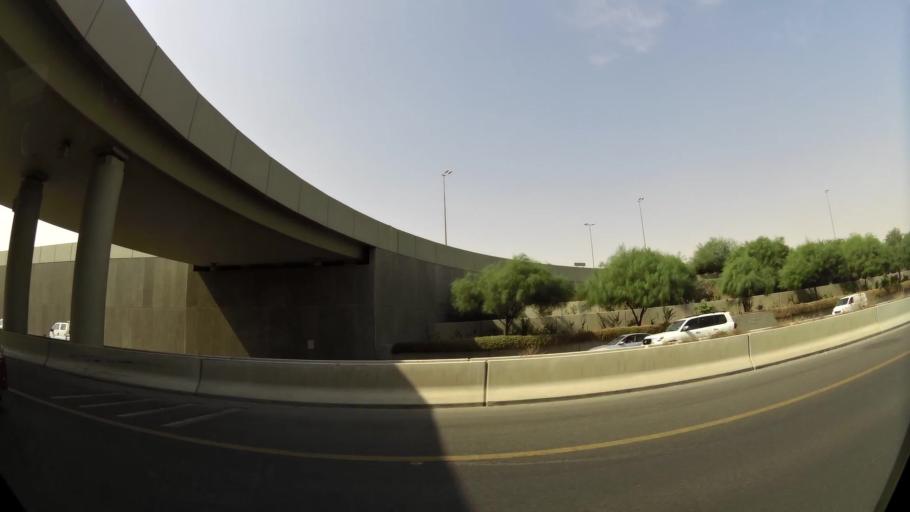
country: KW
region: Al Ahmadi
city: Al Manqaf
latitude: 29.1062
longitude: 48.1183
